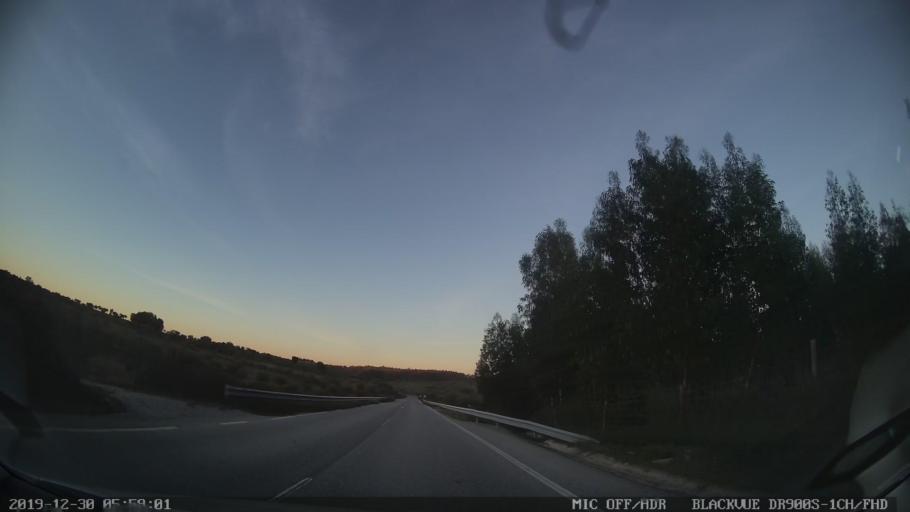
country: PT
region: Castelo Branco
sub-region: Idanha-A-Nova
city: Idanha-a-Nova
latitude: 40.0402
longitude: -7.2421
